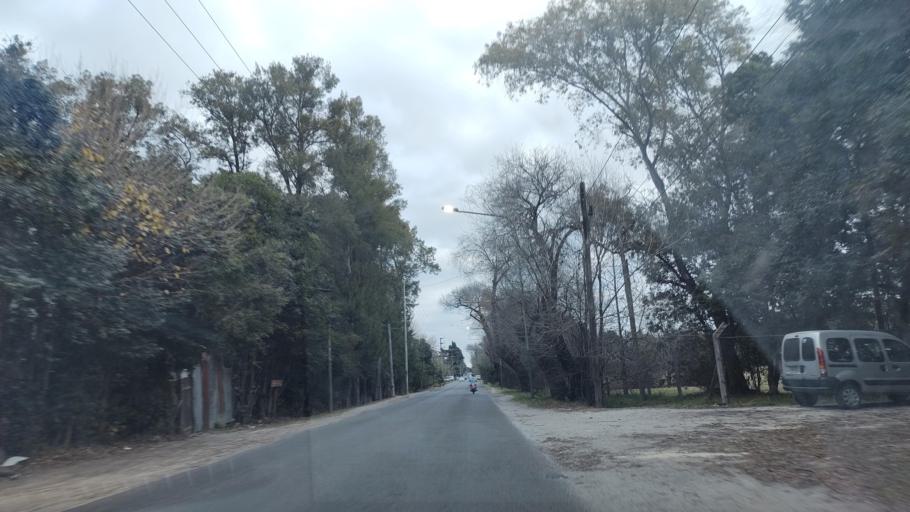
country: AR
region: Buenos Aires
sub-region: Partido de La Plata
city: La Plata
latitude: -34.8650
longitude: -58.0926
